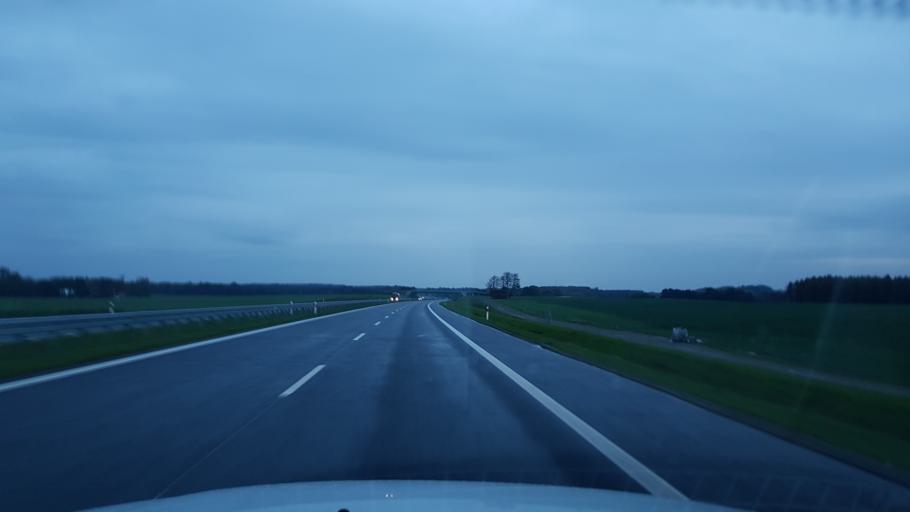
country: PL
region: West Pomeranian Voivodeship
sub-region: Powiat gryficki
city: Brojce
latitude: 53.9202
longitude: 15.3842
